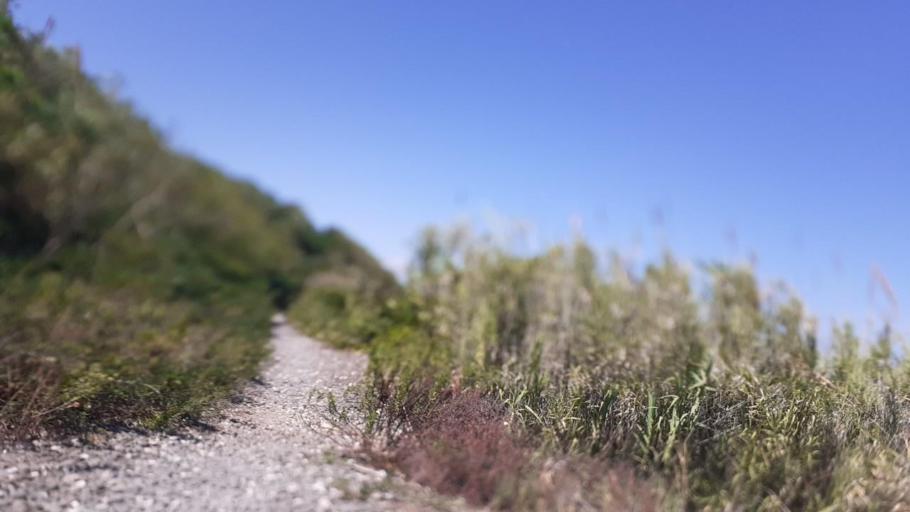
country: IT
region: Abruzzo
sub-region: Provincia di Chieti
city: Torino di Sangro
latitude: 42.2176
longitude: 14.5765
